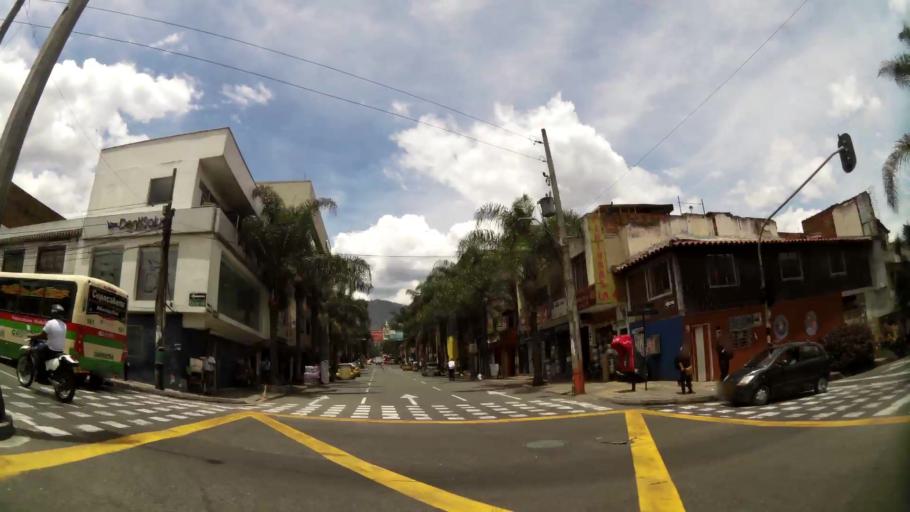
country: CO
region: Antioquia
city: Bello
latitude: 6.3321
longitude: -75.5564
